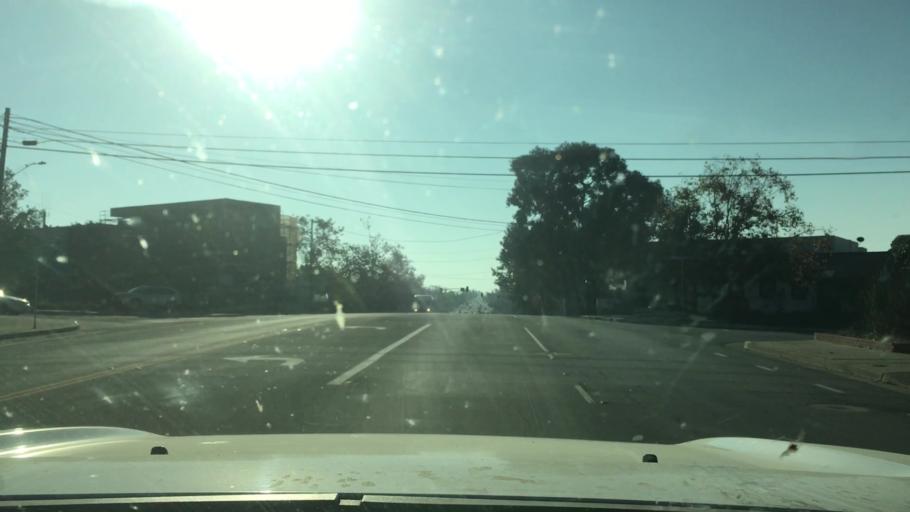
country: US
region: California
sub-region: San Luis Obispo County
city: San Luis Obispo
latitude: 35.2715
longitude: -120.6580
